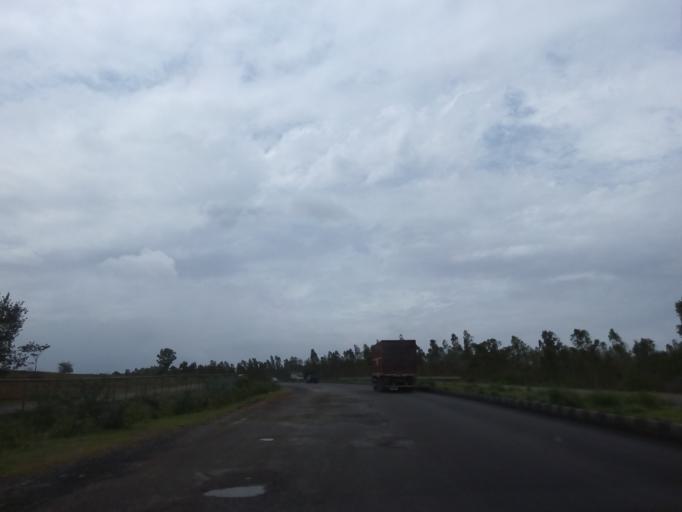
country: IN
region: Karnataka
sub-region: Haveri
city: Byadgi
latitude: 14.7128
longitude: 75.5032
